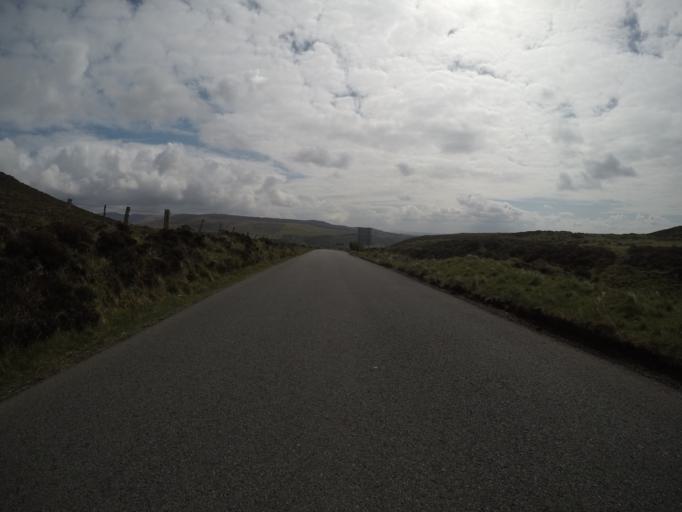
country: GB
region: Scotland
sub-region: Highland
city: Portree
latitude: 57.5951
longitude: -6.3739
